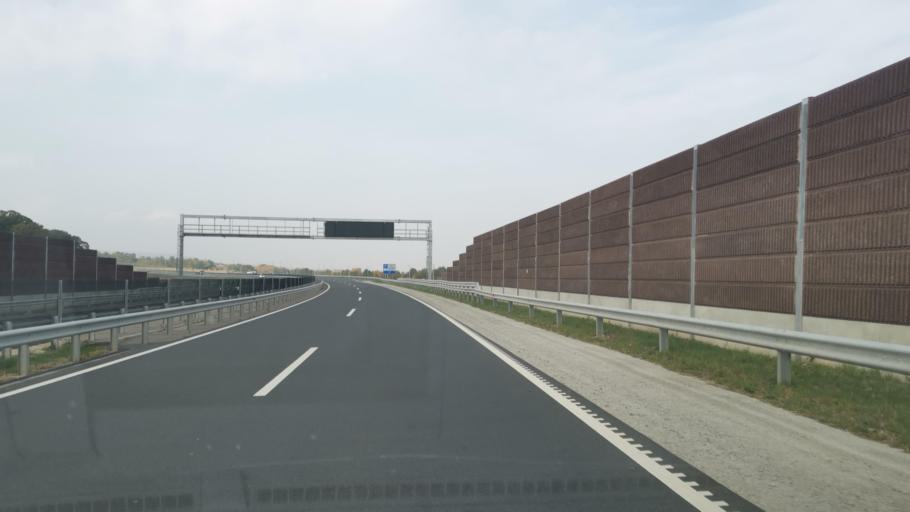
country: AT
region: Burgenland
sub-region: Politischer Bezirk Oberpullendorf
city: Deutschkreutz
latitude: 47.6245
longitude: 16.6529
